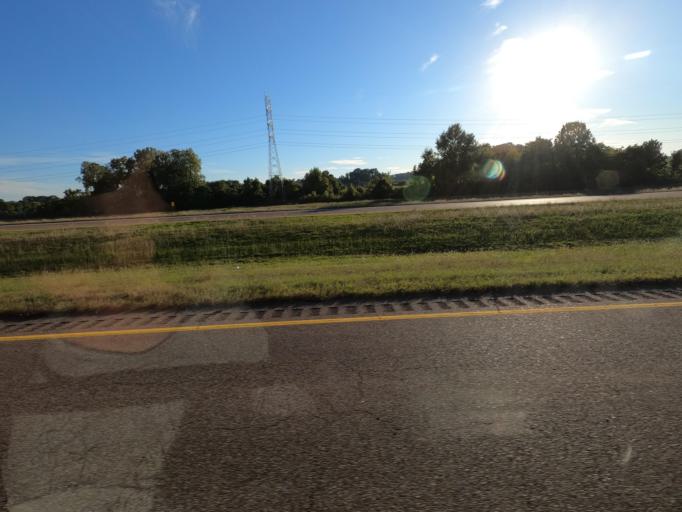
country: US
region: Tennessee
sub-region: Shelby County
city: Millington
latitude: 35.3209
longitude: -89.8761
